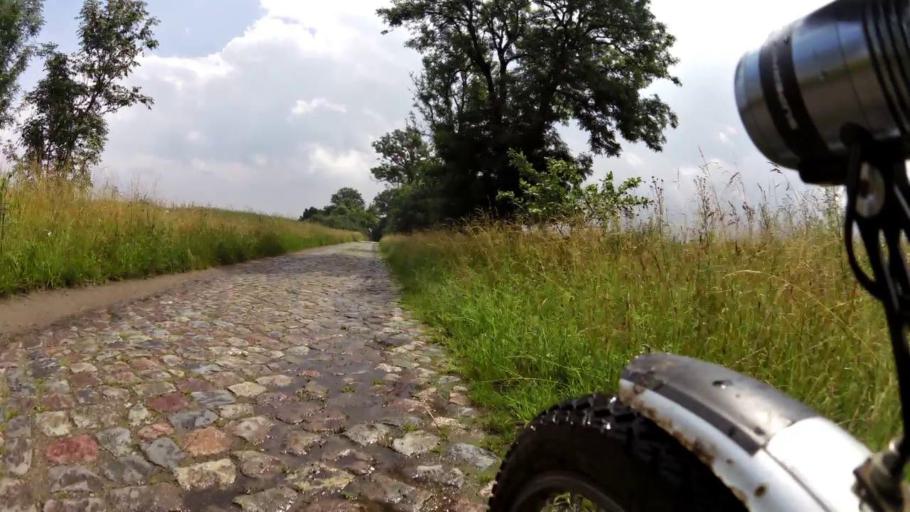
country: PL
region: West Pomeranian Voivodeship
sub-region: Powiat lobeski
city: Lobez
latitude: 53.7314
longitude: 15.6751
